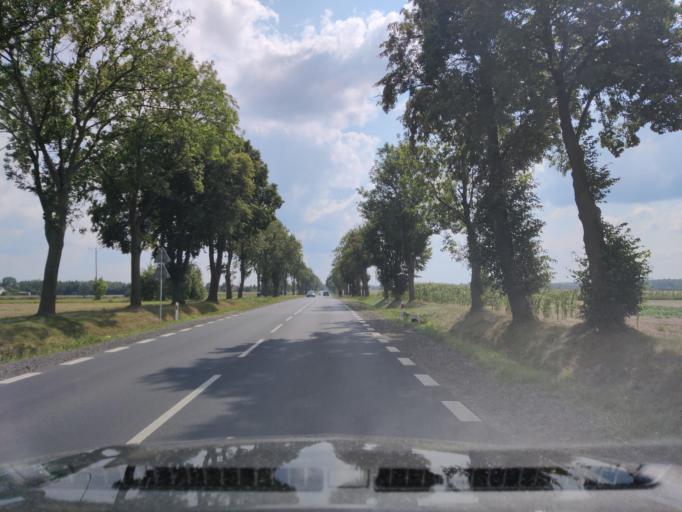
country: PL
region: Masovian Voivodeship
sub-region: Powiat pultuski
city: Zatory
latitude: 52.6139
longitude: 21.1045
